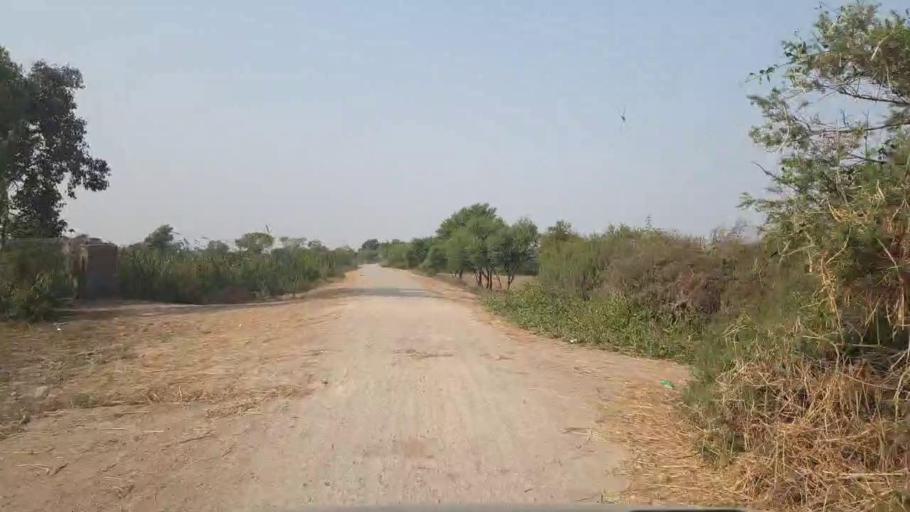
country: PK
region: Sindh
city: Tando Muhammad Khan
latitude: 25.0804
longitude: 68.3436
